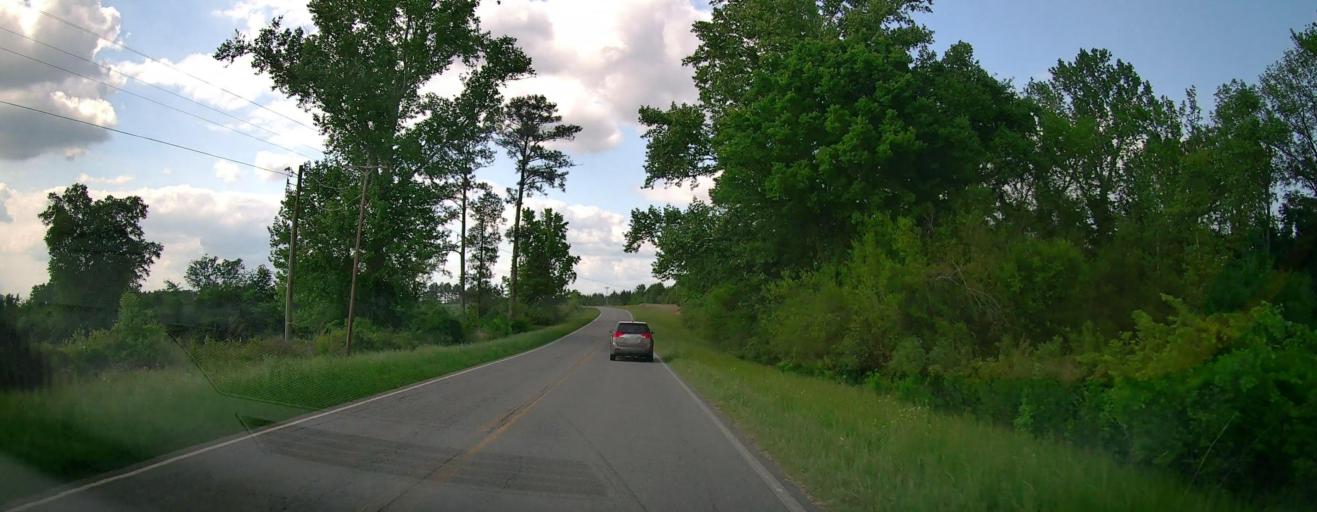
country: US
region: Georgia
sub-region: Laurens County
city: East Dublin
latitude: 32.6119
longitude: -82.8687
